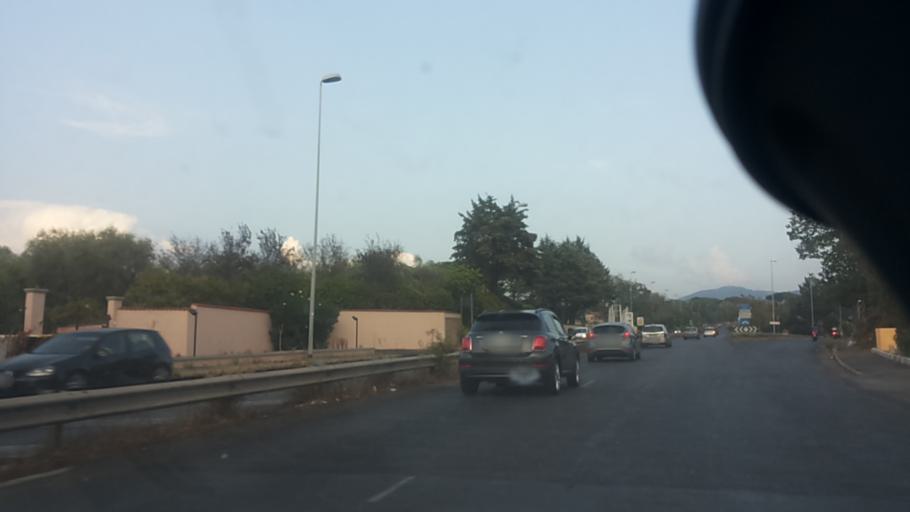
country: IT
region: Latium
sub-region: Citta metropolitana di Roma Capitale
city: Frascati
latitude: 41.8232
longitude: 12.6366
